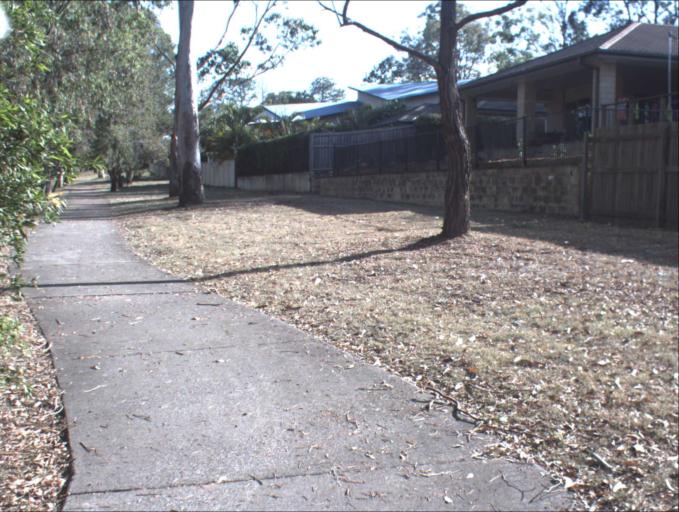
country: AU
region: Queensland
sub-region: Logan
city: Beenleigh
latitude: -27.6754
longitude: 153.2060
